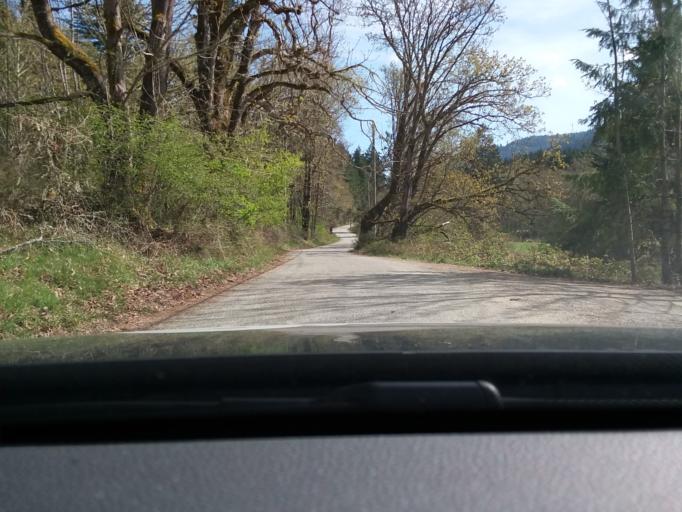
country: CA
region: British Columbia
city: North Saanich
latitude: 48.7907
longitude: -123.5060
